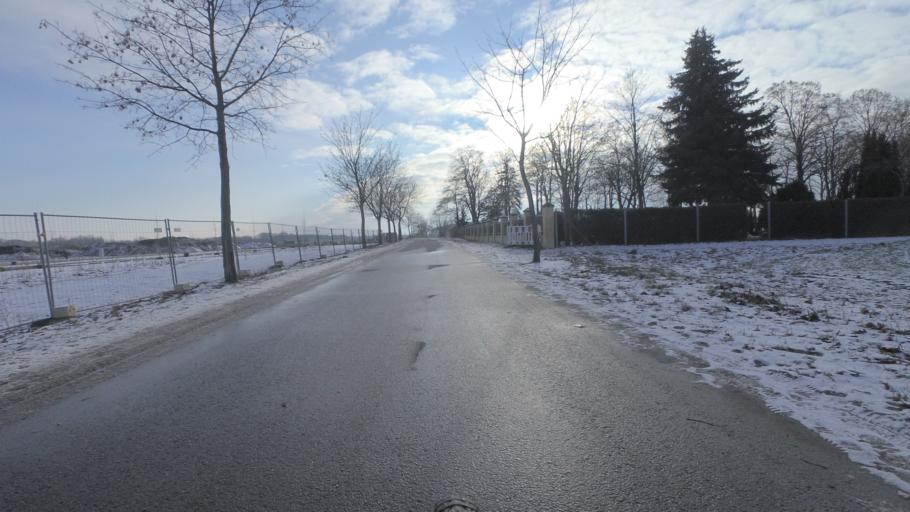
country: DE
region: Brandenburg
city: Zossen
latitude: 52.2396
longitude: 13.4247
